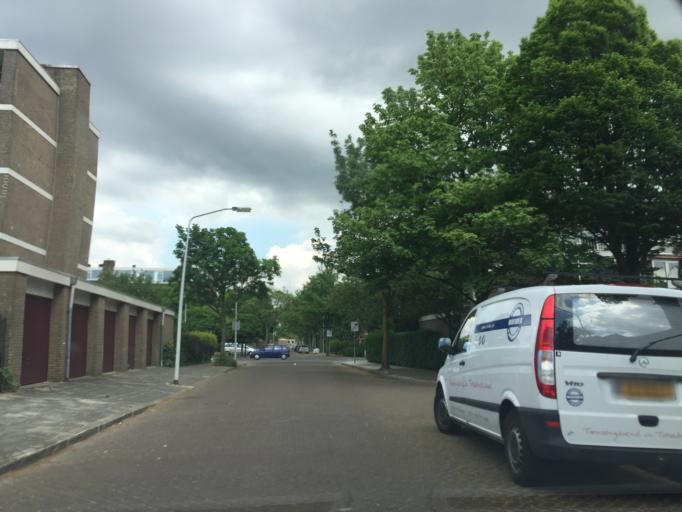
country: NL
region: South Holland
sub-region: Gemeente Leiden
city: Leiden
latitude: 52.1459
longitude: 4.4703
